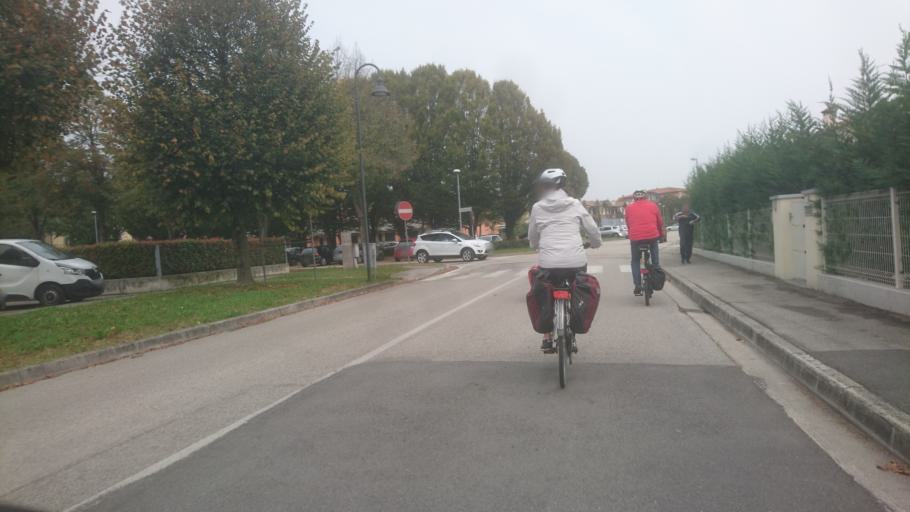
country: IT
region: Veneto
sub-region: Provincia di Vicenza
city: Camisano Vicentino
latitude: 45.5246
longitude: 11.7118
